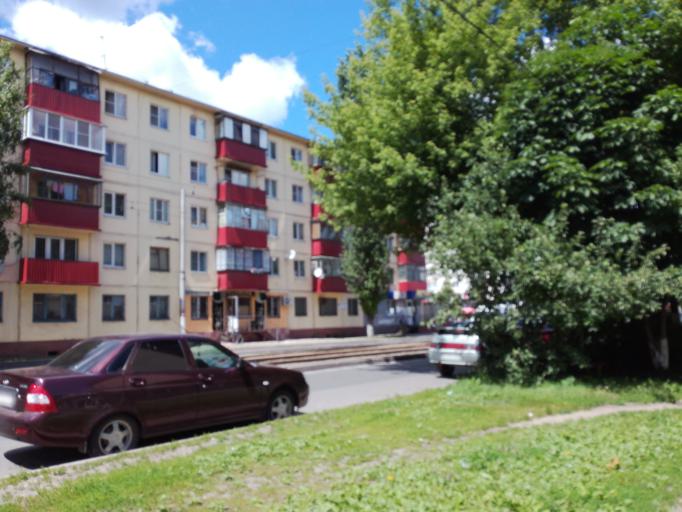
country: RU
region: Kursk
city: Kursk
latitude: 51.7458
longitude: 36.2469
